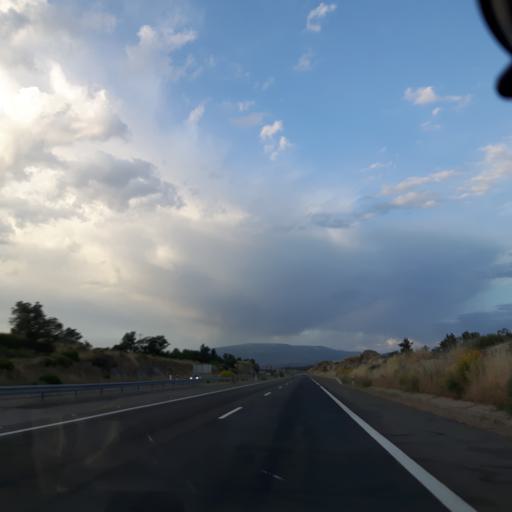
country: ES
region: Castille and Leon
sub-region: Provincia de Salamanca
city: Fuentes de Bejar
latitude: 40.5186
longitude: -5.6730
